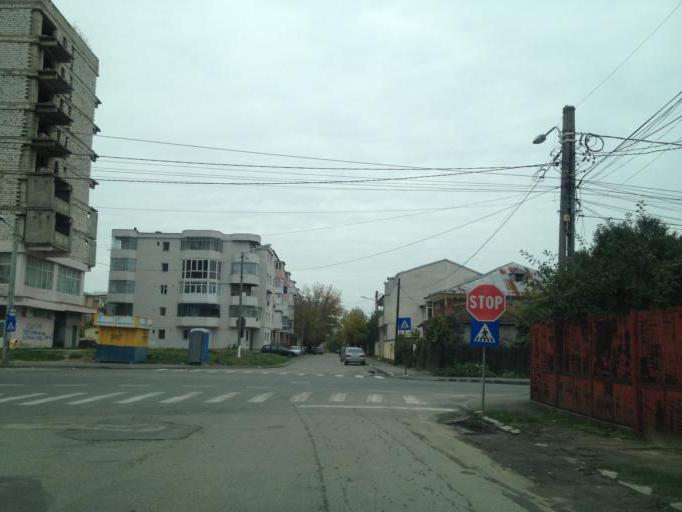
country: RO
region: Dolj
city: Craiova
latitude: 44.3329
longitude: 23.7781
